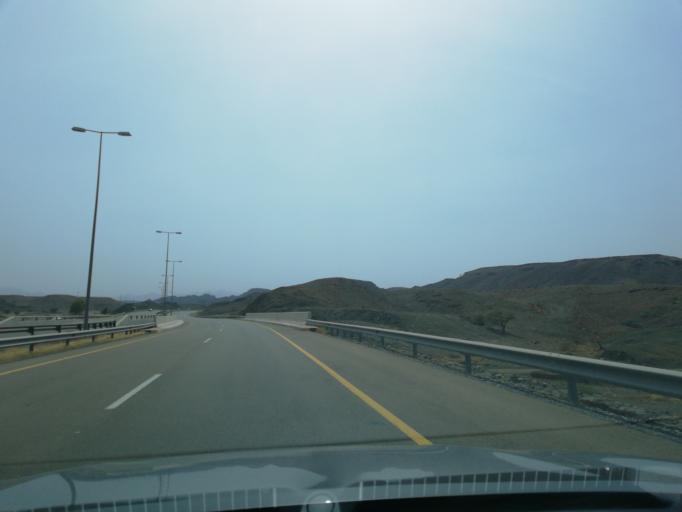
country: OM
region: Al Batinah
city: Al Liwa'
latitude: 24.3202
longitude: 56.4652
